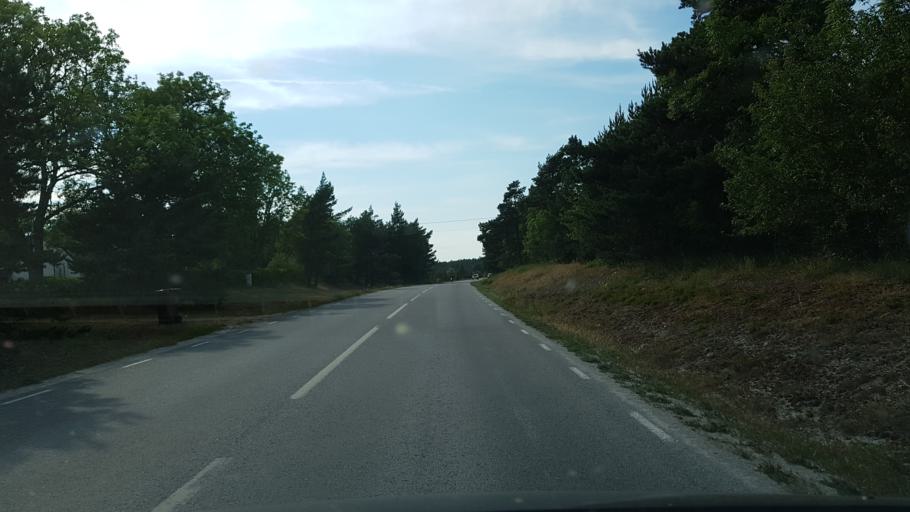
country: SE
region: Gotland
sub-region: Gotland
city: Visby
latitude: 57.6318
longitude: 18.4148
